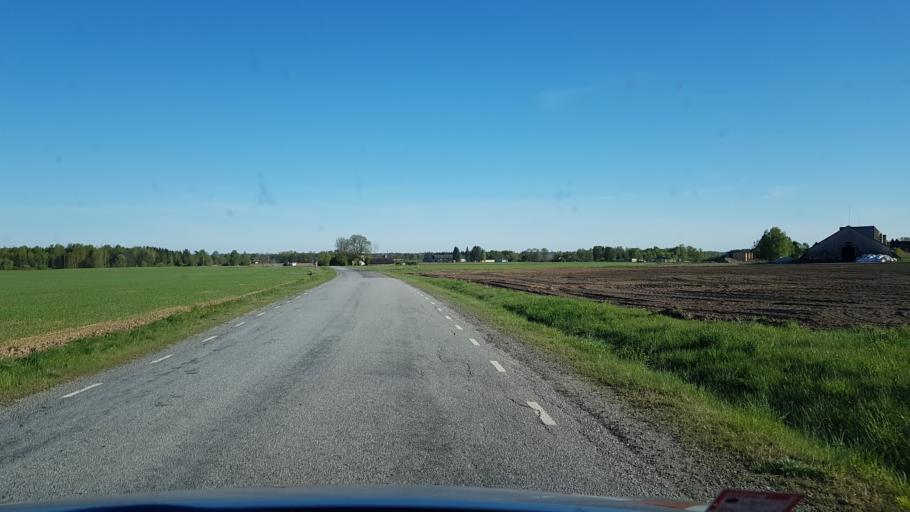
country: EE
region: Vorumaa
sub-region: Voru linn
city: Voru
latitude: 57.9228
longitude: 26.9509
